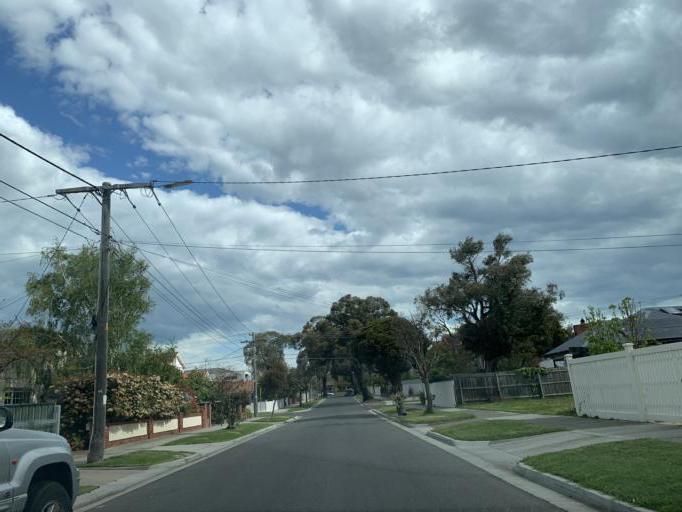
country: AU
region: Victoria
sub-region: Bayside
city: Hampton
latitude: -37.9347
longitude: 145.0132
